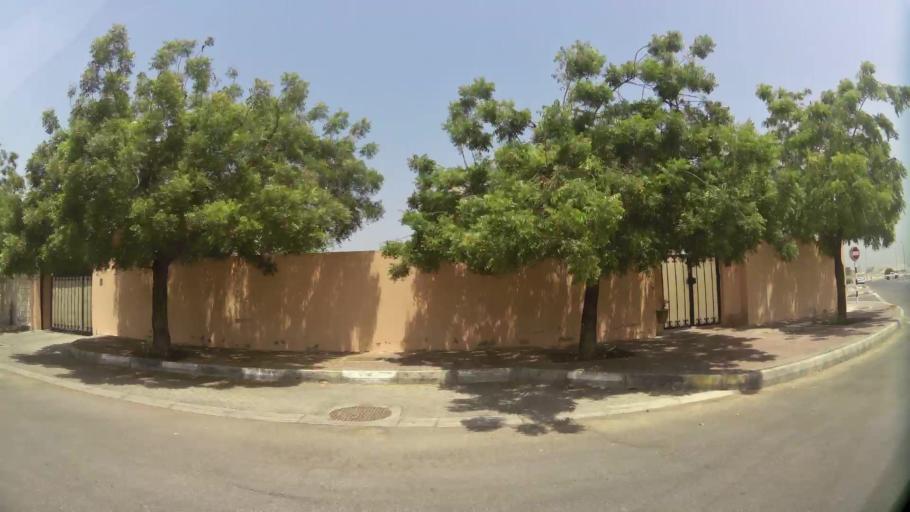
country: AE
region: Ash Shariqah
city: Sharjah
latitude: 25.3453
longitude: 55.3742
